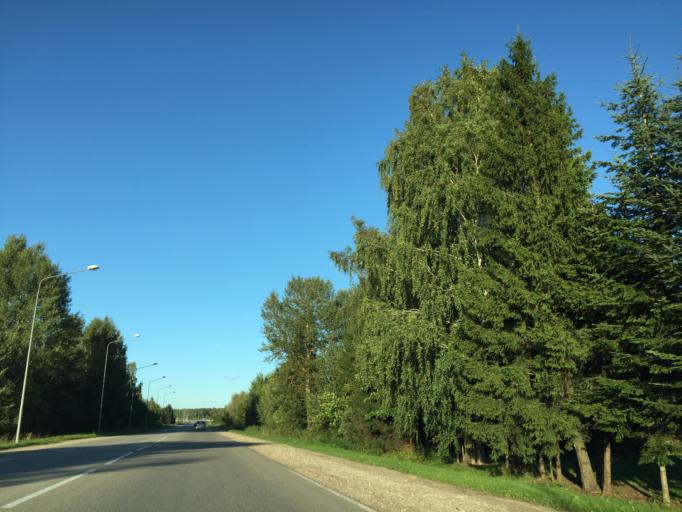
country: LV
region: Kuldigas Rajons
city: Kuldiga
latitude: 56.9591
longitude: 21.9936
